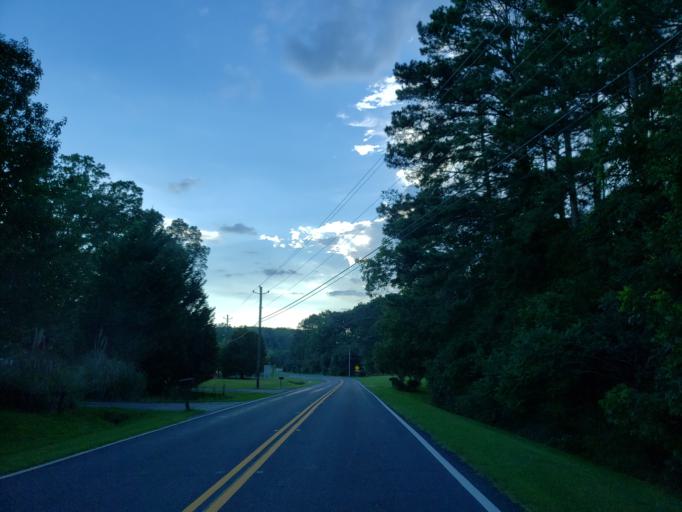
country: US
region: Georgia
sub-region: Bartow County
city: Cartersville
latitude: 34.2073
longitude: -84.7513
